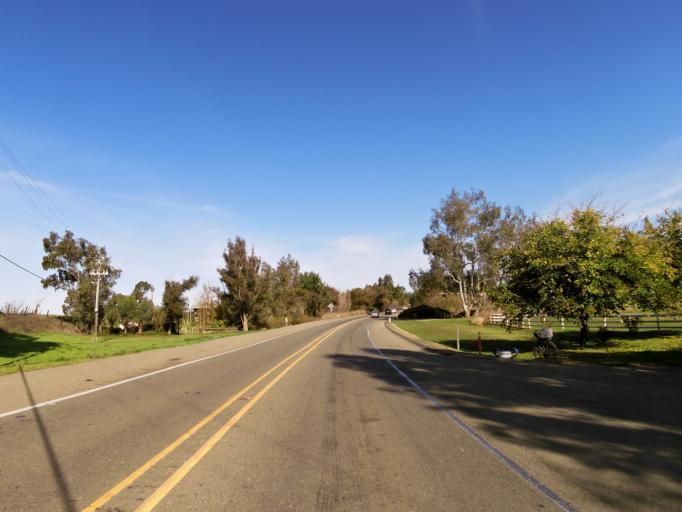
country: US
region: California
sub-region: Solano County
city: Rio Vista
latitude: 38.0986
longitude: -121.7060
